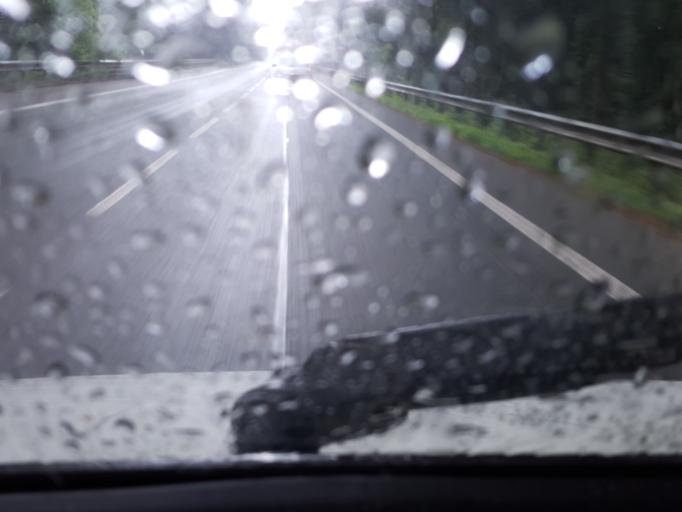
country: DE
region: North Rhine-Westphalia
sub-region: Regierungsbezirk Detmold
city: Petershagen
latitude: 52.3432
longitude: 8.9421
